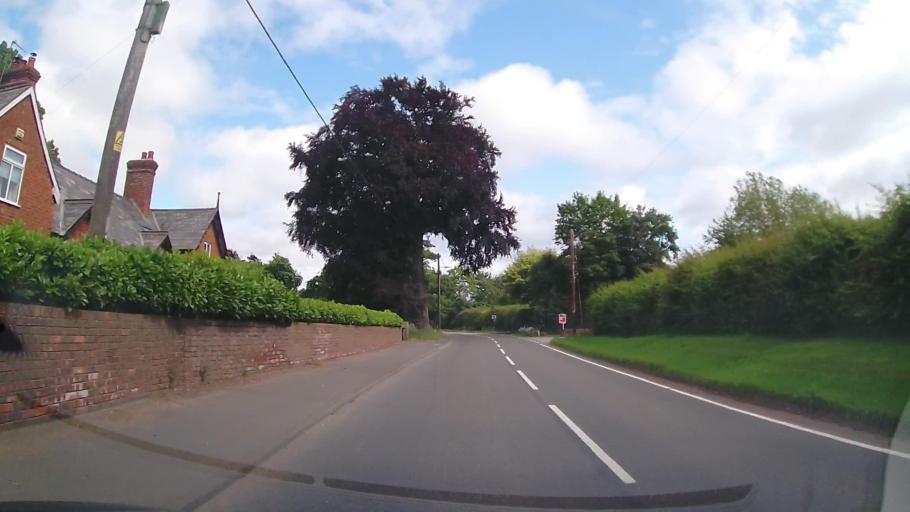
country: GB
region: England
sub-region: Shropshire
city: Whittington
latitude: 52.7933
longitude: -2.9843
